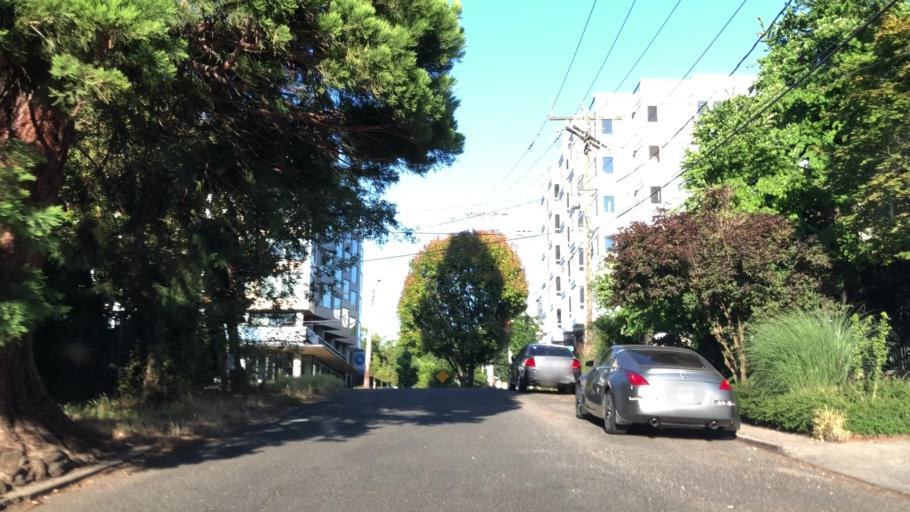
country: US
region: Washington
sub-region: King County
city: Seattle
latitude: 47.6211
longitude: -122.3227
